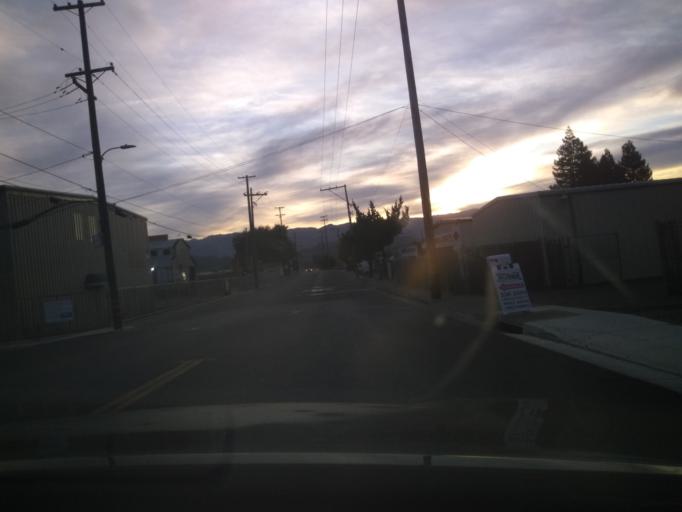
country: US
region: California
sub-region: Mendocino County
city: Ukiah
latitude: 39.1592
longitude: -123.2076
